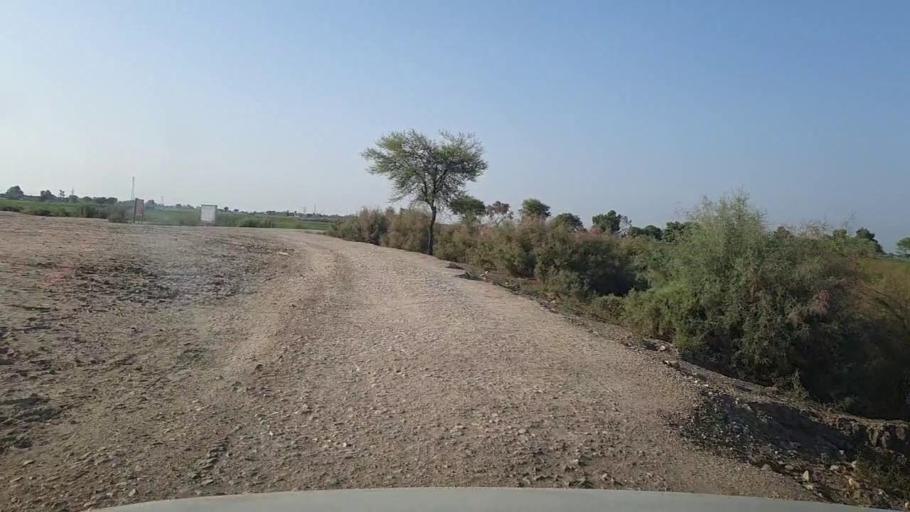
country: PK
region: Sindh
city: Kandhkot
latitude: 28.2977
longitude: 69.3292
